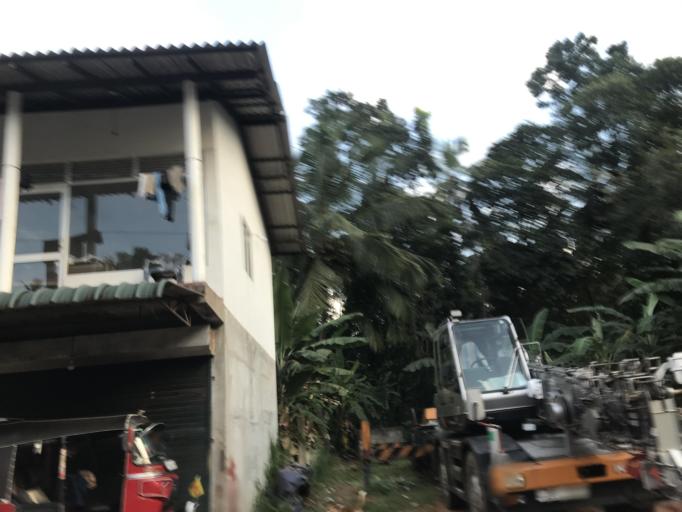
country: LK
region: Western
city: Gampaha
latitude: 7.1019
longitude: 79.9761
